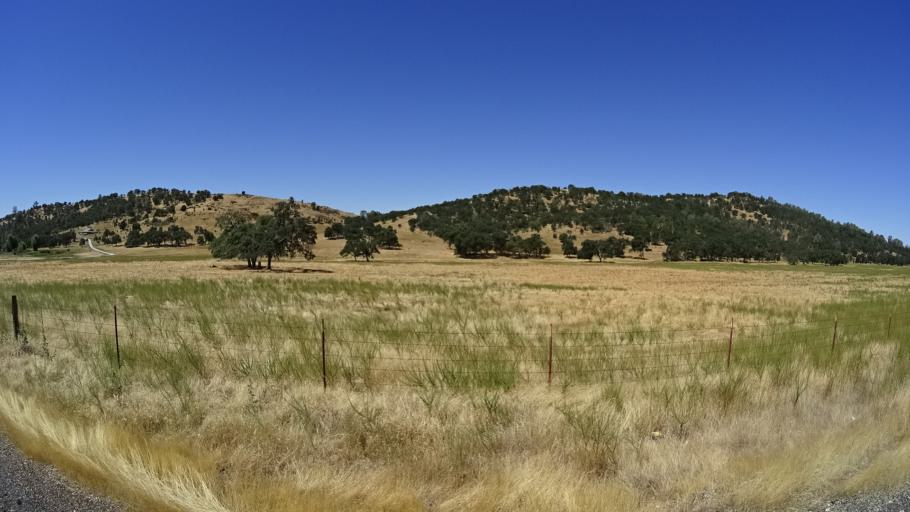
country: US
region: California
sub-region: Calaveras County
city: Copperopolis
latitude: 37.9911
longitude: -120.6513
